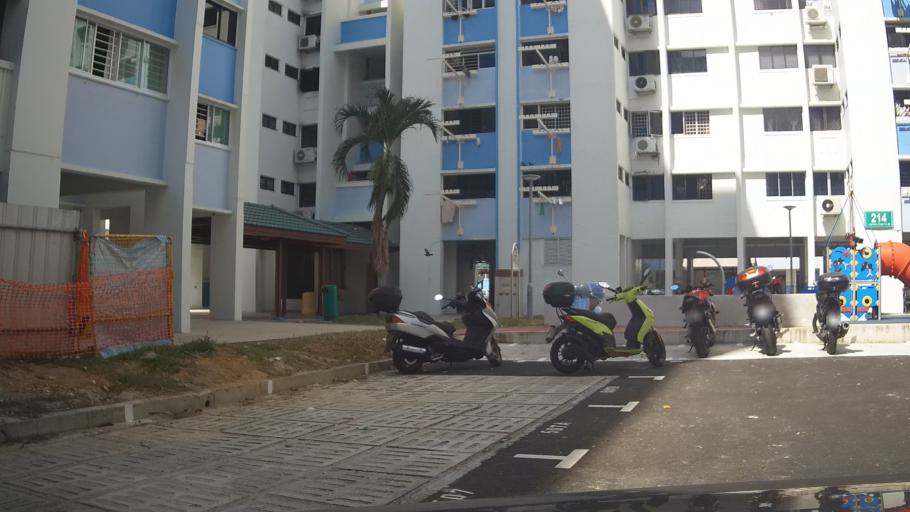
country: SG
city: Singapore
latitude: 1.3546
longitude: 103.9538
